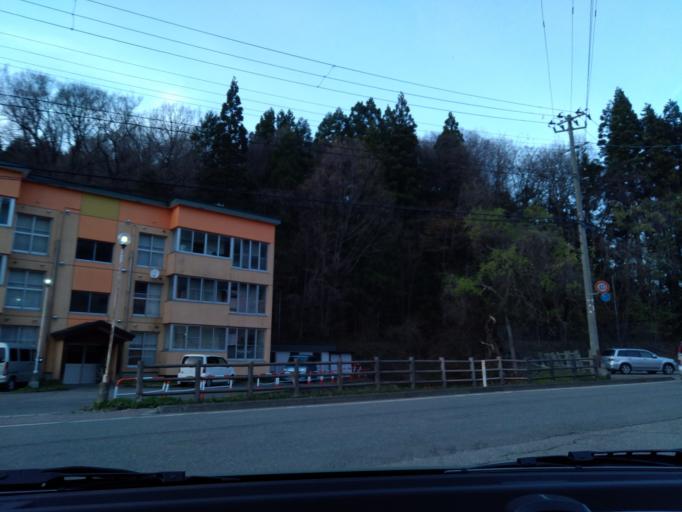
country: JP
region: Akita
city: Kakunodatemachi
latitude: 39.5936
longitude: 140.5810
